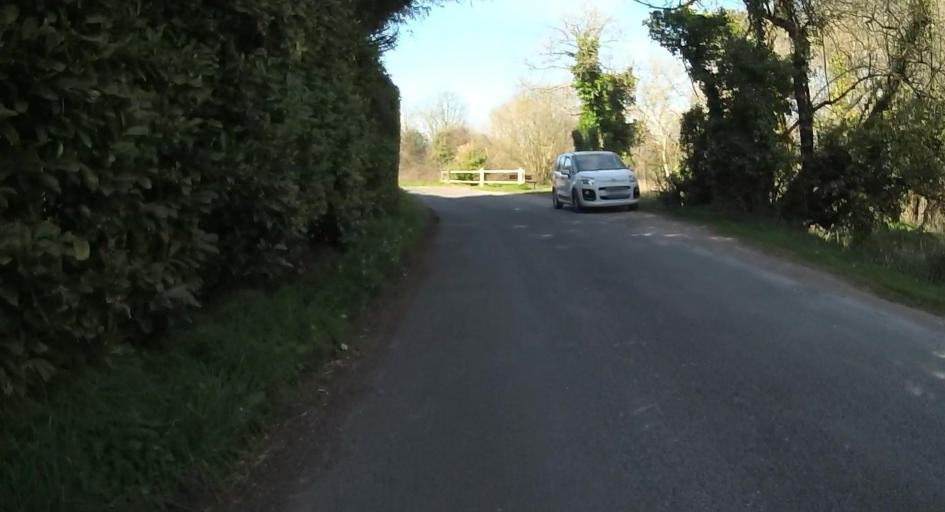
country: GB
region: England
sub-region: Hampshire
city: Abbotts Ann
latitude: 51.1312
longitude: -1.4854
